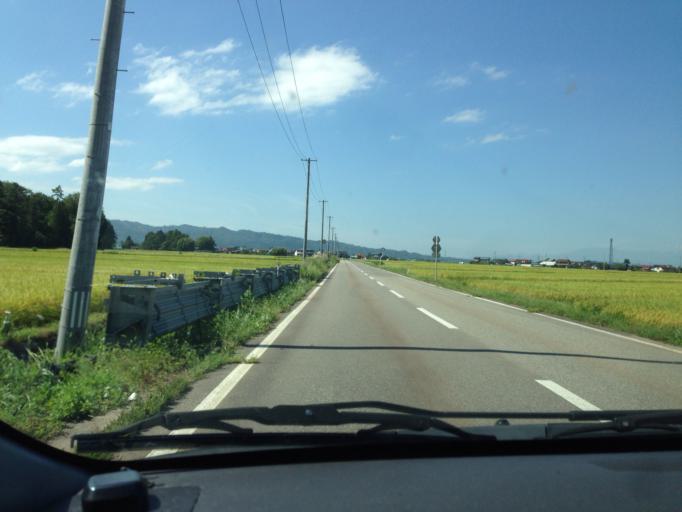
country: JP
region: Fukushima
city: Kitakata
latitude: 37.4370
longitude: 139.8625
